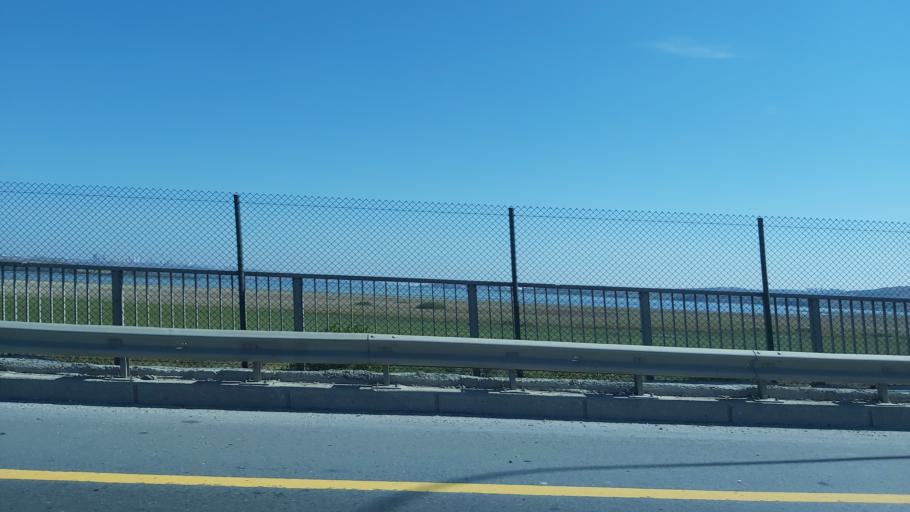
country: TR
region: Istanbul
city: Muratbey
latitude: 41.1049
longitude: 28.5297
